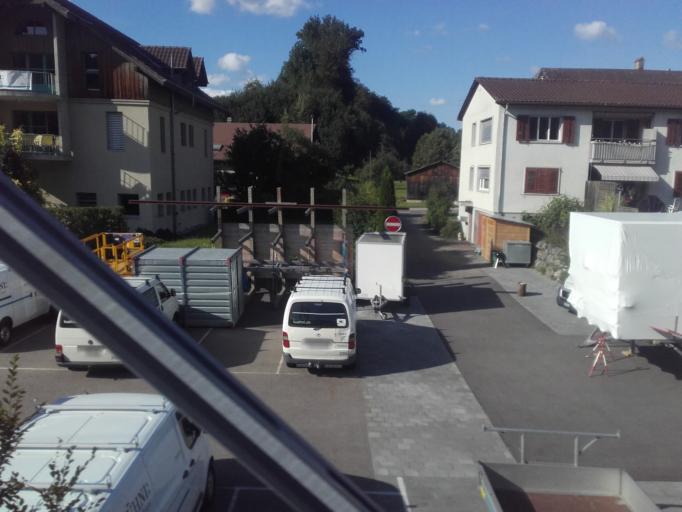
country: CH
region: Bern
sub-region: Emmental District
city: Lutzelfluh
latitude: 46.9973
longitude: 7.7043
